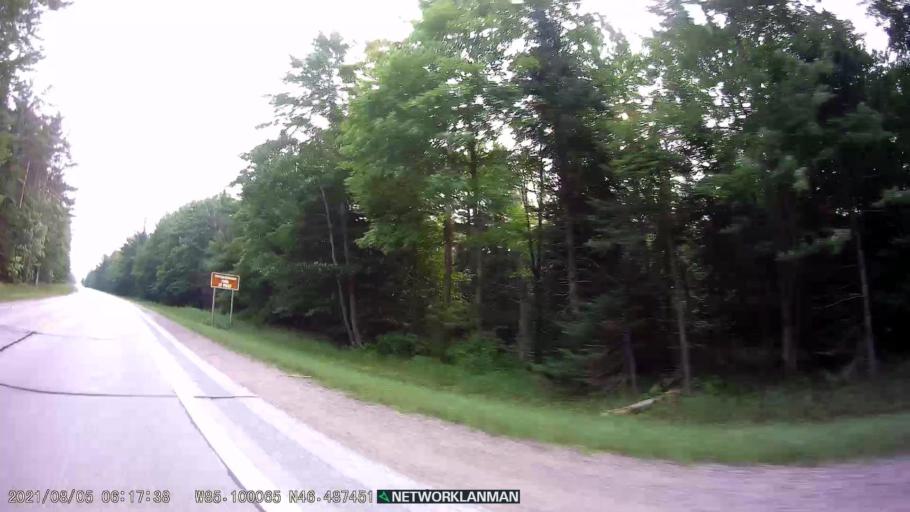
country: US
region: Michigan
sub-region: Luce County
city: Newberry
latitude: 46.4886
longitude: -85.0995
